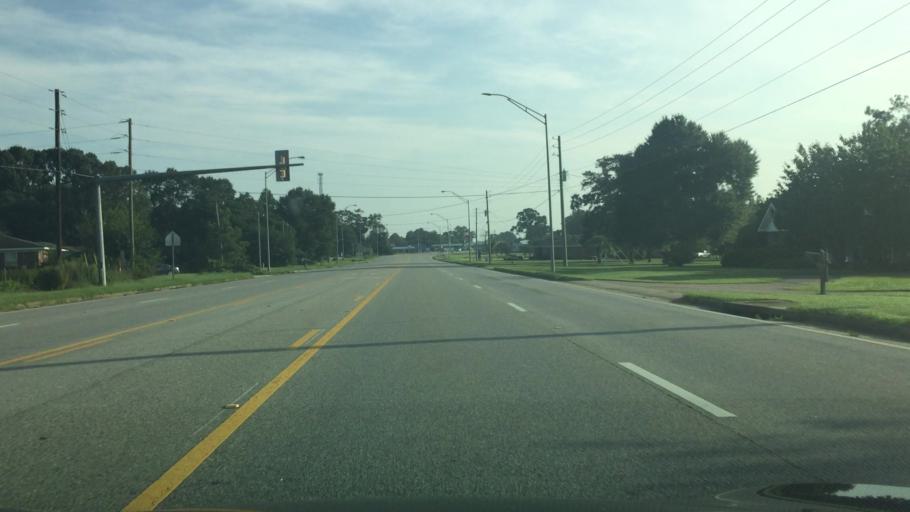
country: US
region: Alabama
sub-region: Covington County
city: Andalusia
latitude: 31.2881
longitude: -86.5037
